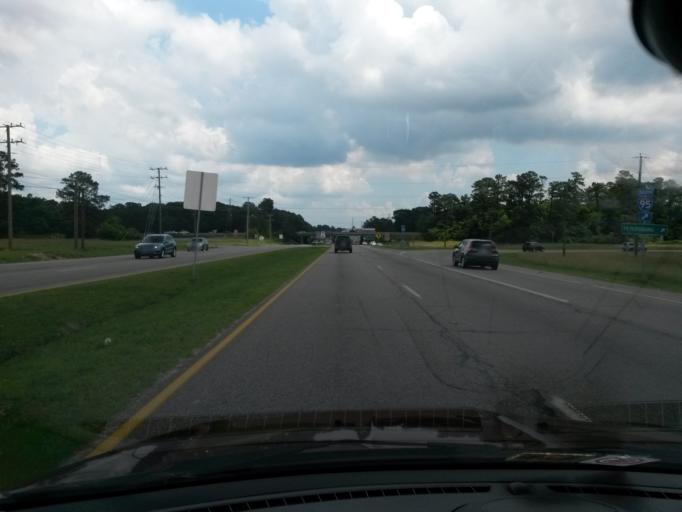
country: US
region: Virginia
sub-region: Chesterfield County
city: Chester
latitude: 37.3547
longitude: -77.4080
